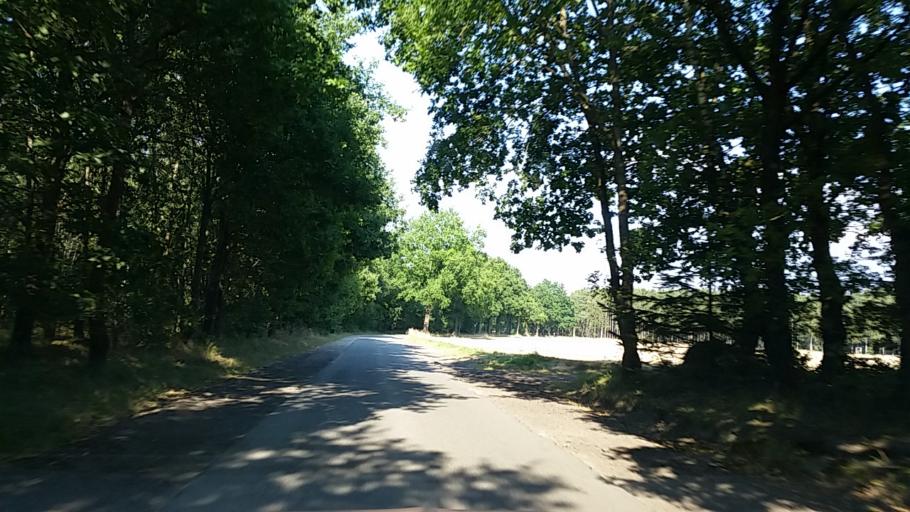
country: DE
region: Lower Saxony
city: Handeloh
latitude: 53.2711
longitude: 9.8849
